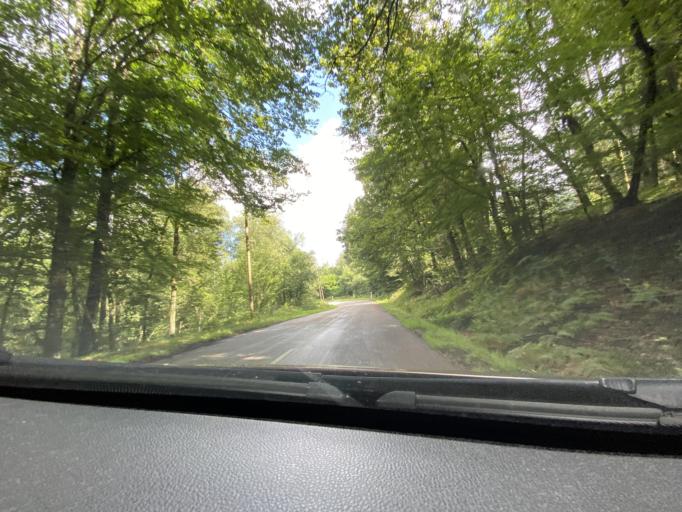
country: FR
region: Bourgogne
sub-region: Departement de la Cote-d'Or
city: Saulieu
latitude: 47.2576
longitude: 4.0772
